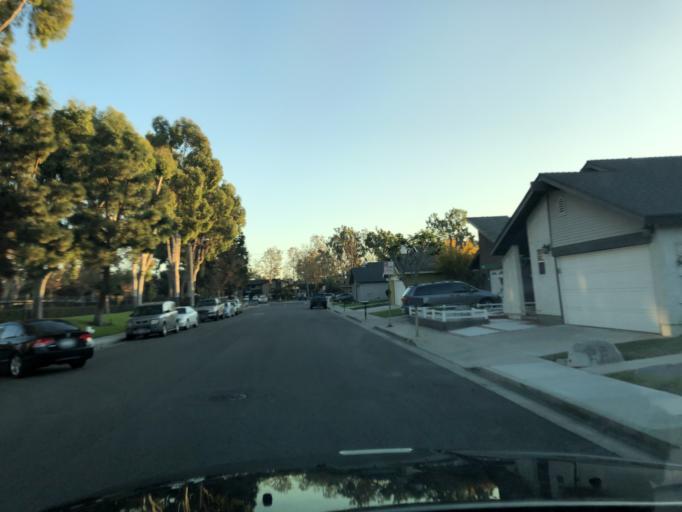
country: US
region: California
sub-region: Orange County
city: Costa Mesa
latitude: 33.6835
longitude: -117.8803
